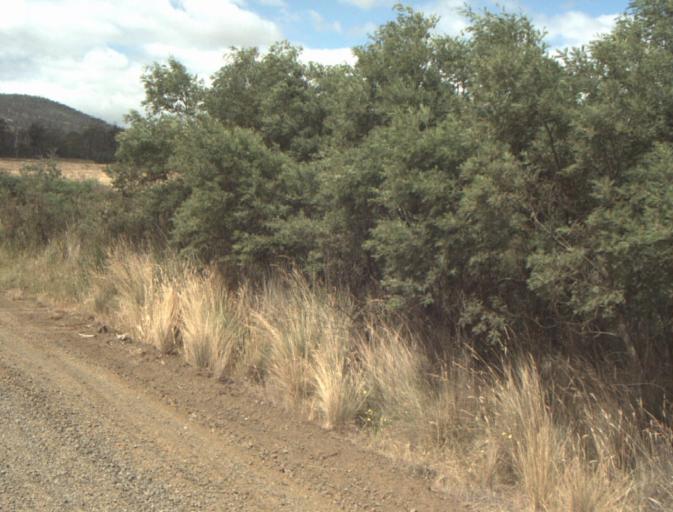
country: AU
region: Tasmania
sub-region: Northern Midlands
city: Evandale
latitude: -41.5162
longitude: 147.3516
